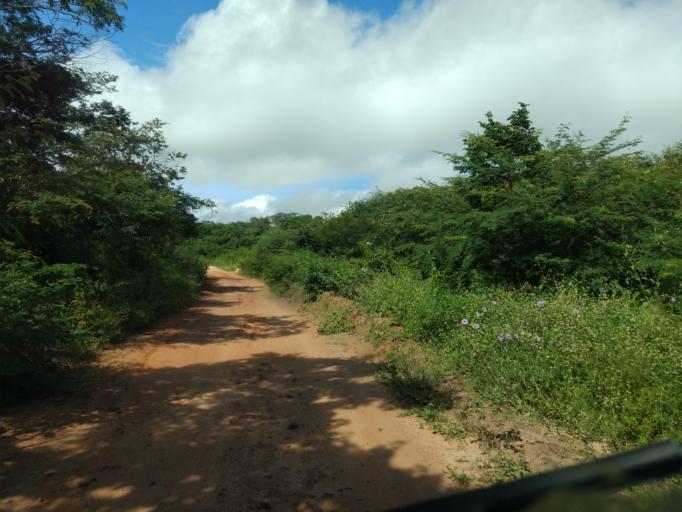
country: BR
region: Ceara
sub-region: Crateus
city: Crateus
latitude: -5.2169
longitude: -40.9473
